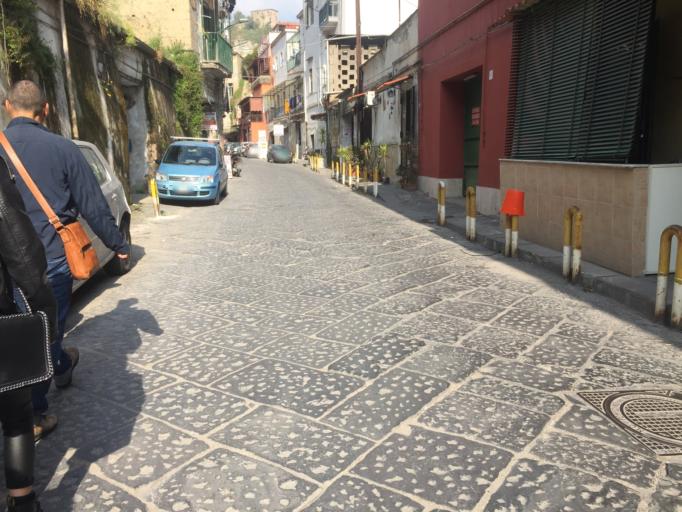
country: IT
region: Campania
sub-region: Provincia di Napoli
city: Napoli
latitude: 40.8586
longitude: 14.2408
